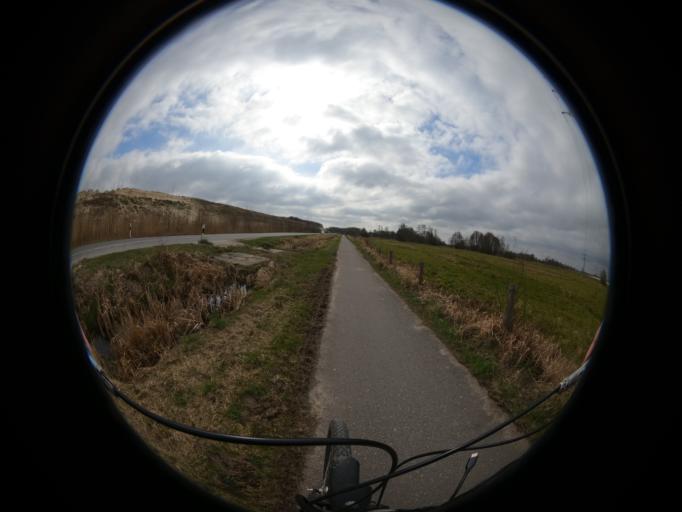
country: DE
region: Lower Saxony
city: Neu Wulmstorf
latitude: 53.4880
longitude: 9.7804
